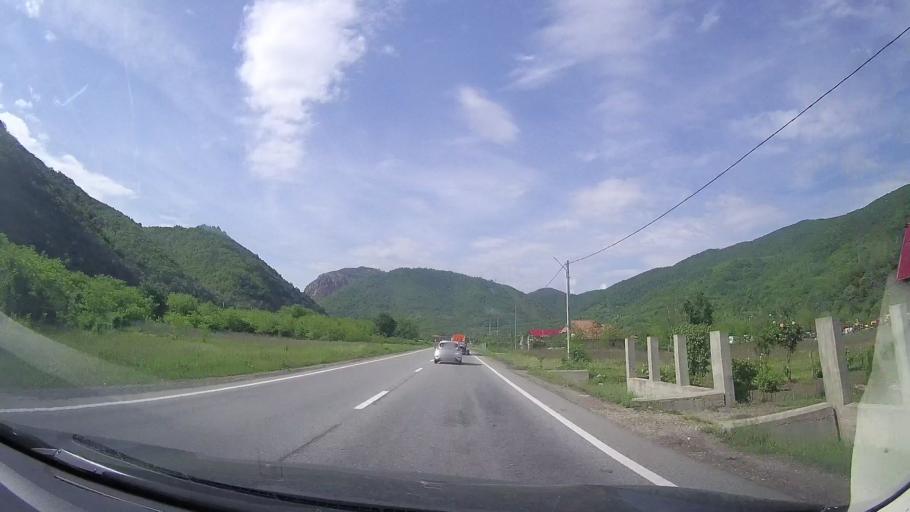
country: RO
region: Caras-Severin
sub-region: Comuna Mehadia
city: Mehadia
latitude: 44.8801
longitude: 22.3839
